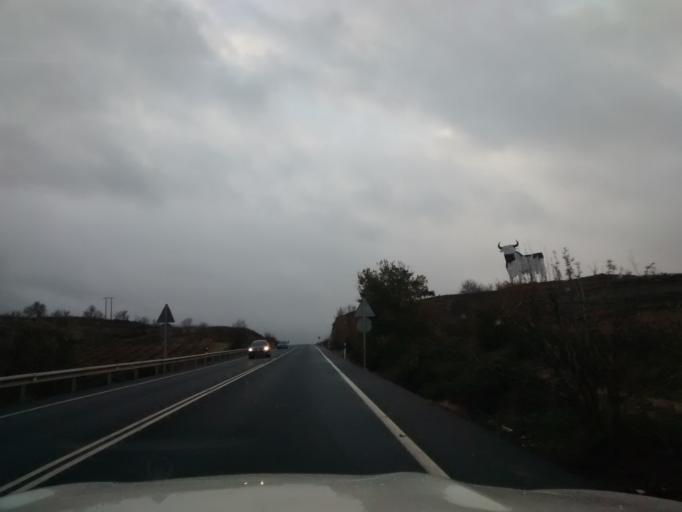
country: ES
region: La Rioja
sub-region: Provincia de La Rioja
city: San Asensio
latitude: 42.5106
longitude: -2.7209
